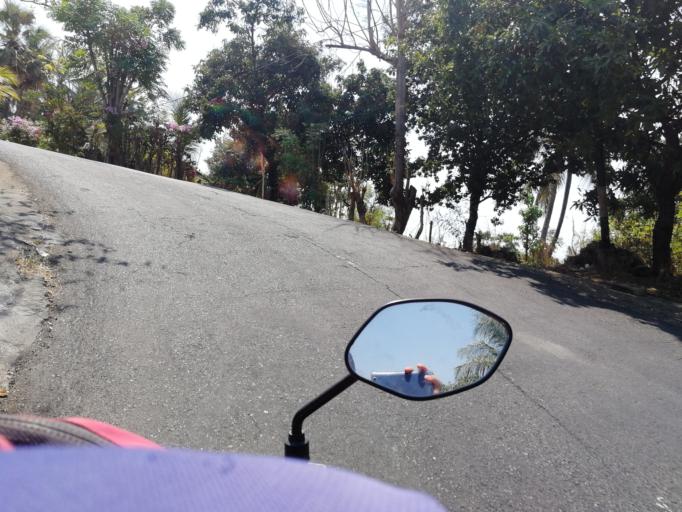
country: ID
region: Bali
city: Banjar Trunyan
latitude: -8.1273
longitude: 115.3261
